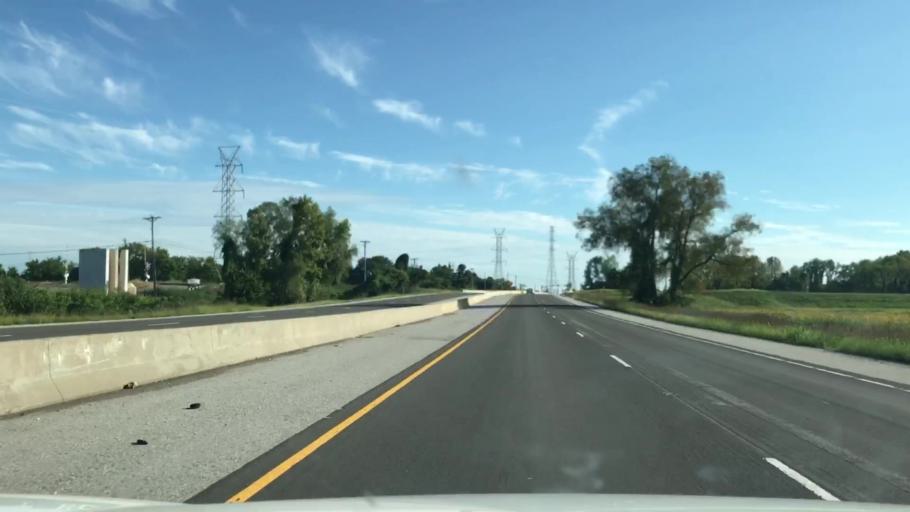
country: US
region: Illinois
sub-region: Madison County
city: Hartford
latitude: 38.8083
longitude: -90.0989
